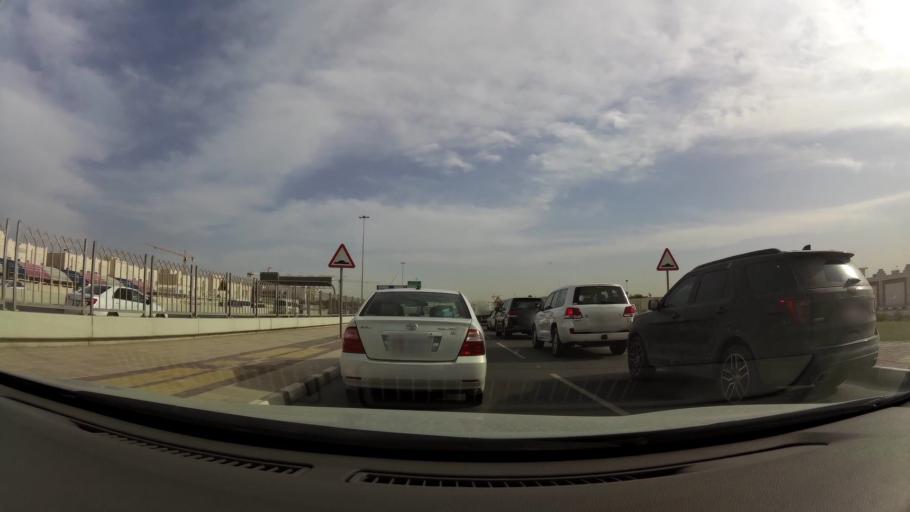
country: QA
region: Baladiyat ar Rayyan
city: Ar Rayyan
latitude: 25.3054
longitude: 51.4729
